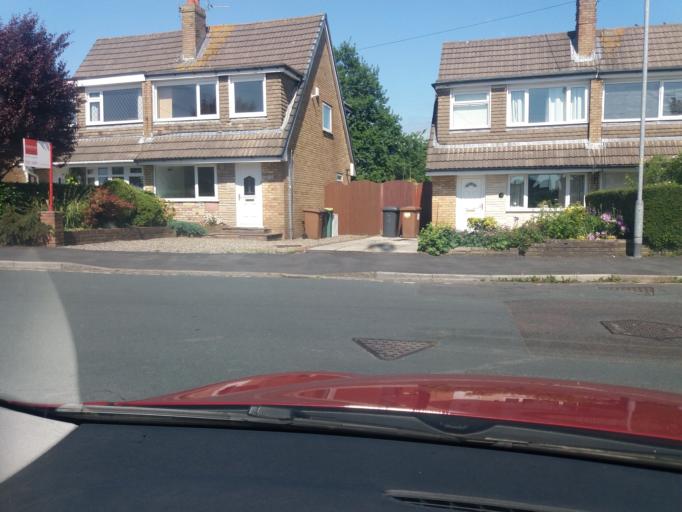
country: GB
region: England
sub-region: Lancashire
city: Preston
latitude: 53.7949
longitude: -2.7050
